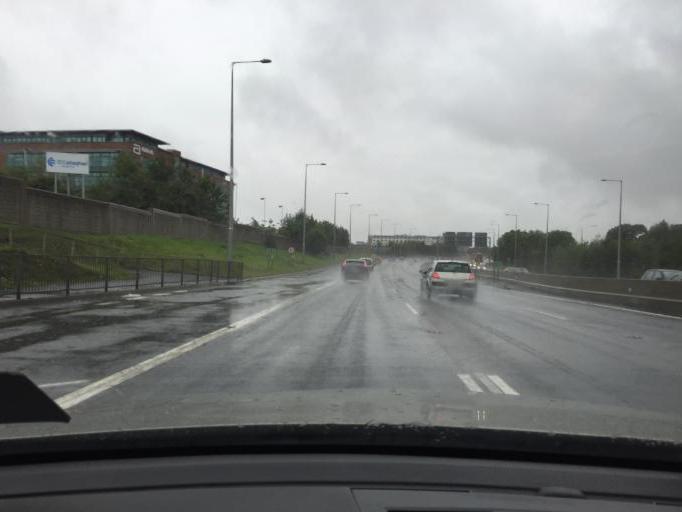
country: IE
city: Palmerstown
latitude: 53.3558
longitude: -6.3923
